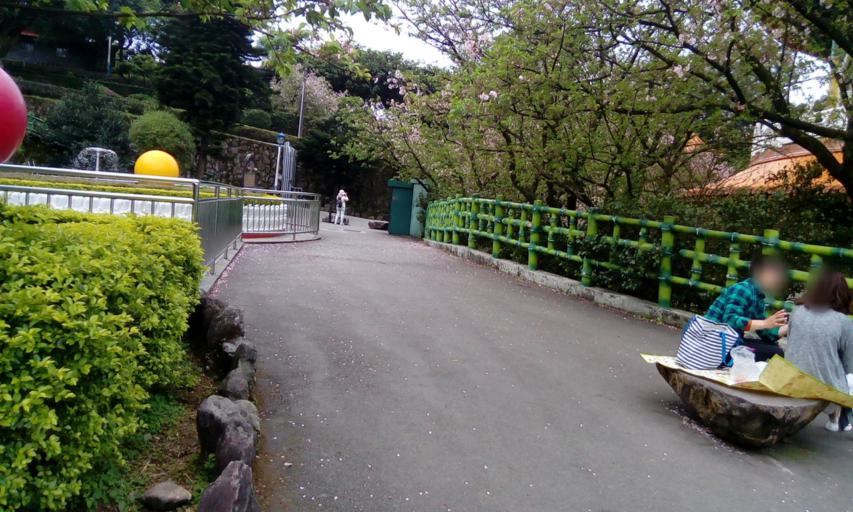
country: TW
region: Taipei
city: Taipei
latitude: 25.1856
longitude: 121.4866
